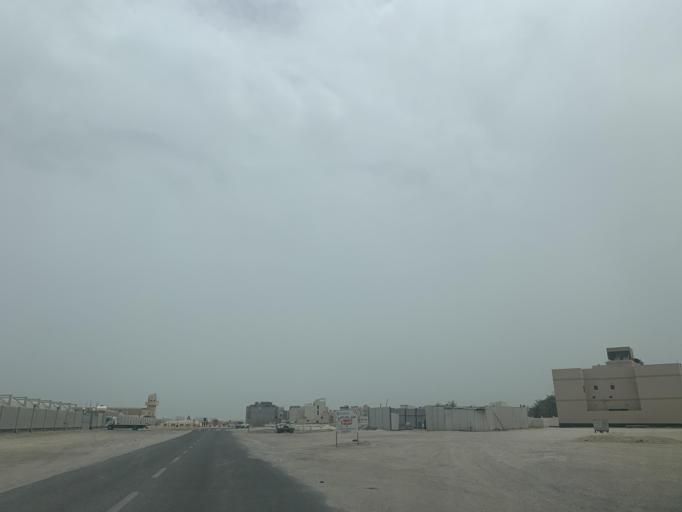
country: BH
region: Northern
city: Sitrah
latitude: 26.1747
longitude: 50.6233
